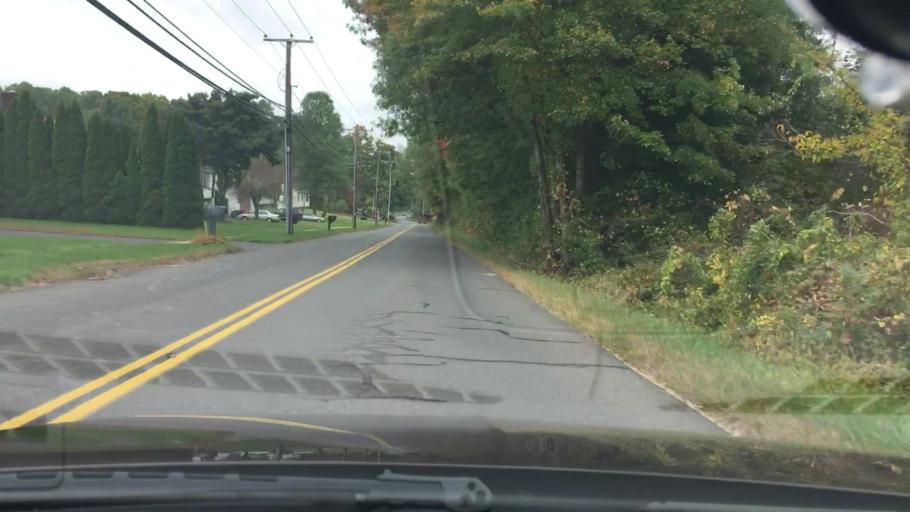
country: US
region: Connecticut
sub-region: Hartford County
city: Hazardville
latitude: 42.0073
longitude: -72.5128
